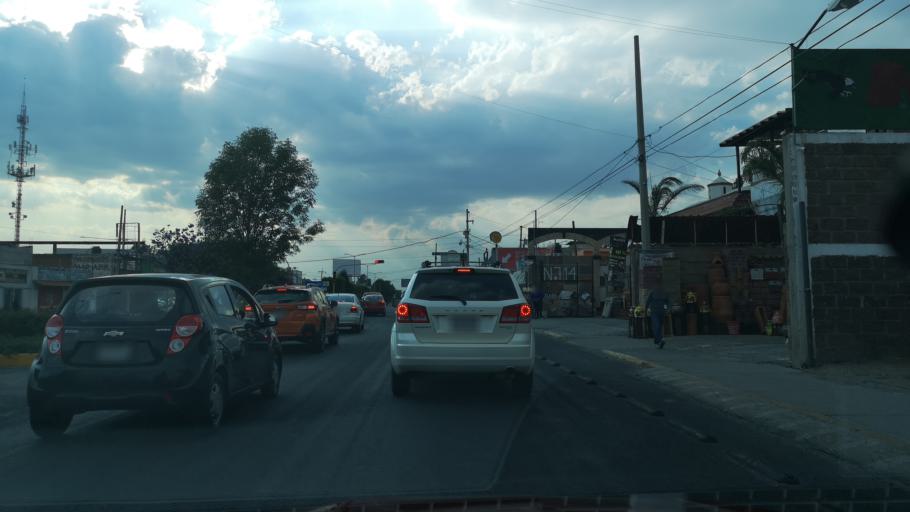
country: MX
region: Puebla
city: Cholula
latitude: 19.0692
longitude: -98.3101
